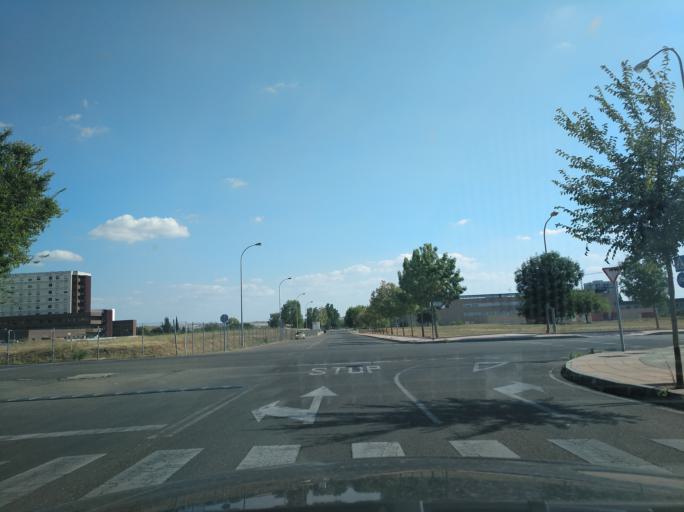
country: ES
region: Extremadura
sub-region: Provincia de Badajoz
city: Badajoz
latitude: 38.8864
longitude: -7.0034
